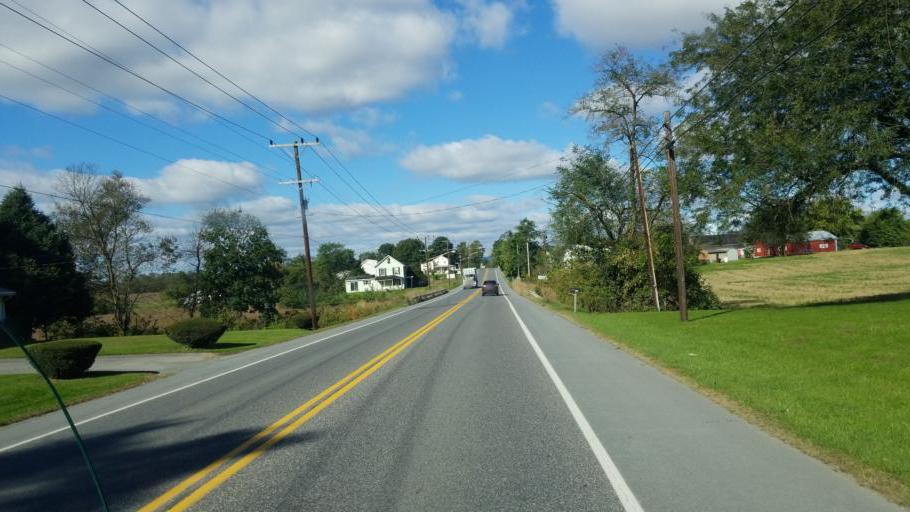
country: US
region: Pennsylvania
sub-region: Franklin County
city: Greencastle
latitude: 39.8034
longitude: -77.8000
